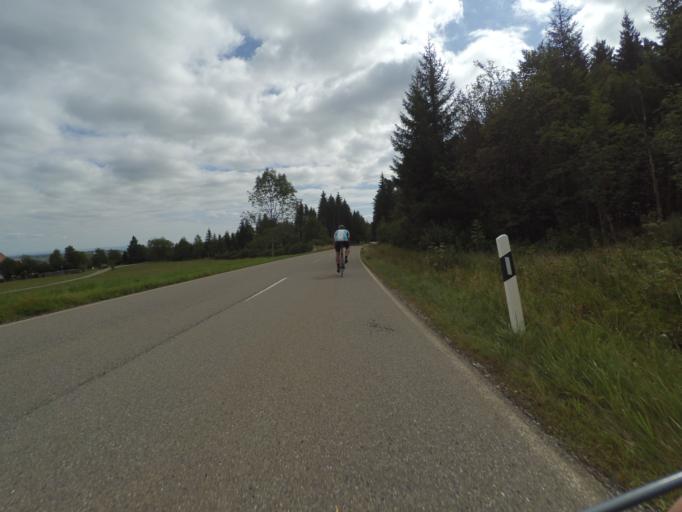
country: DE
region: Baden-Wuerttemberg
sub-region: Freiburg Region
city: Lenzkirch
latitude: 47.8300
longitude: 8.2499
